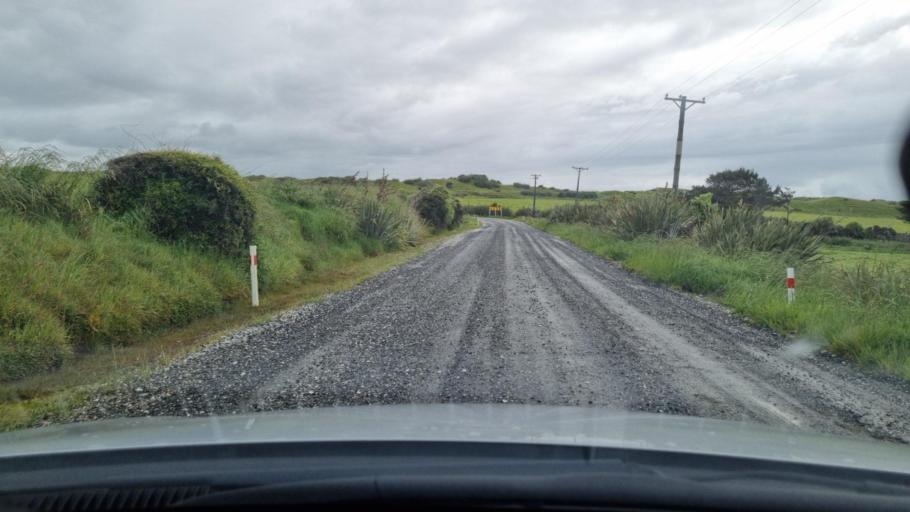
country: NZ
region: Southland
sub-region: Invercargill City
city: Bluff
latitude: -46.5214
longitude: 168.2721
